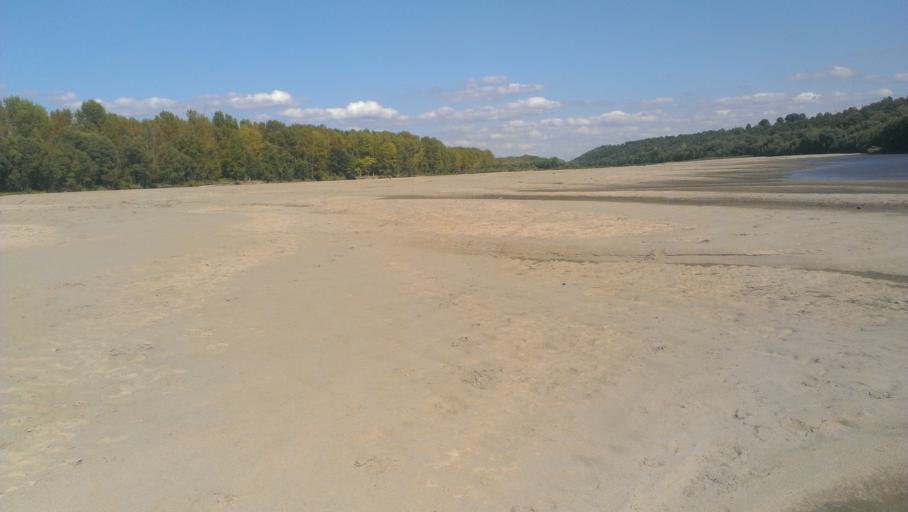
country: RU
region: Altai Krai
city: Nauchnyy Gorodok
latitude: 53.4306
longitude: 83.5083
